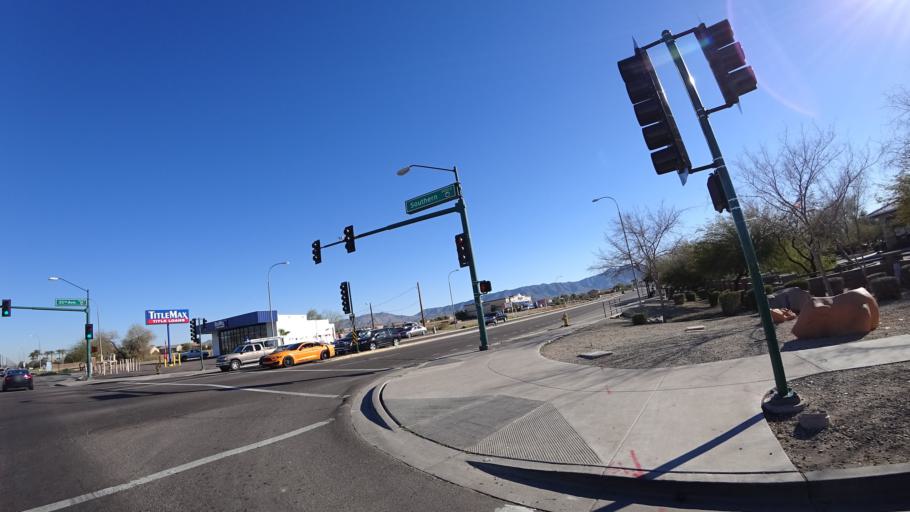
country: US
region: Arizona
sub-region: Maricopa County
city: Laveen
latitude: 33.3920
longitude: -112.1338
